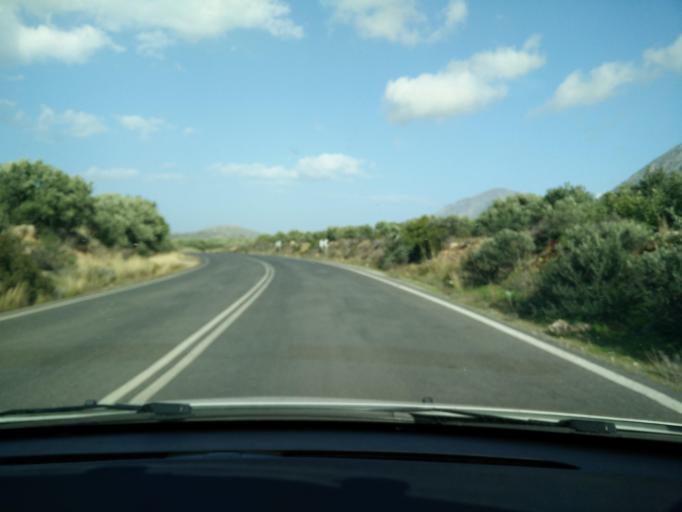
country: GR
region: Crete
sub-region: Nomos Lasithiou
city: Kato Chorio
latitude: 35.0842
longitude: 25.8156
